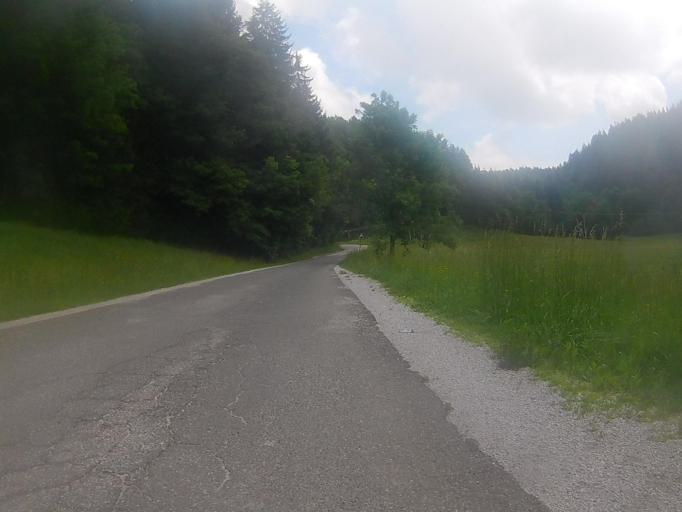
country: SI
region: Maribor
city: Bresternica
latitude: 46.6194
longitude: 15.5543
